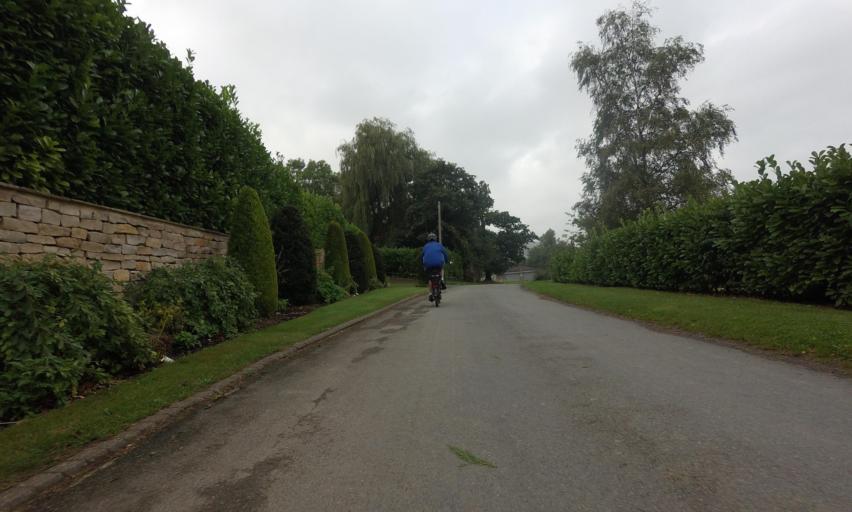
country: GB
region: England
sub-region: Gloucestershire
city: Gotherington
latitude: 51.9747
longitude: -2.0268
